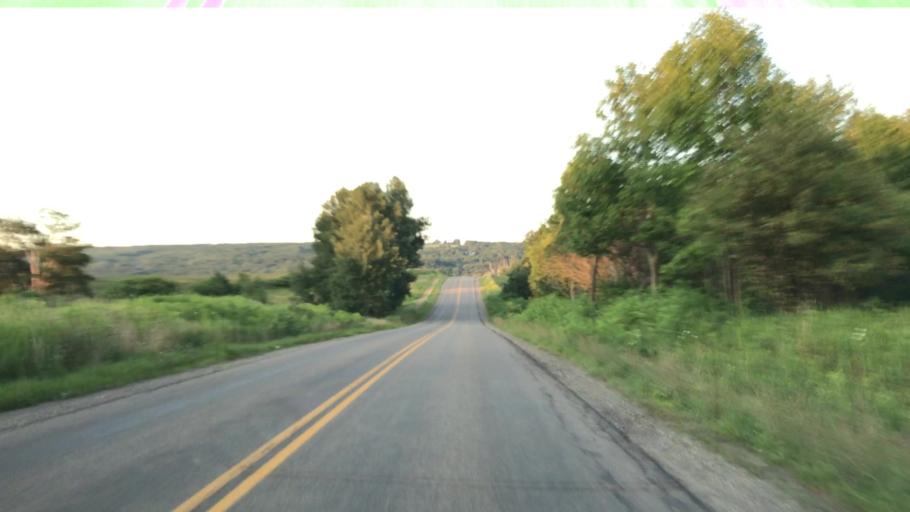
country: US
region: New York
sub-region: Chautauqua County
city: Brocton
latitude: 42.3105
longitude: -79.3739
